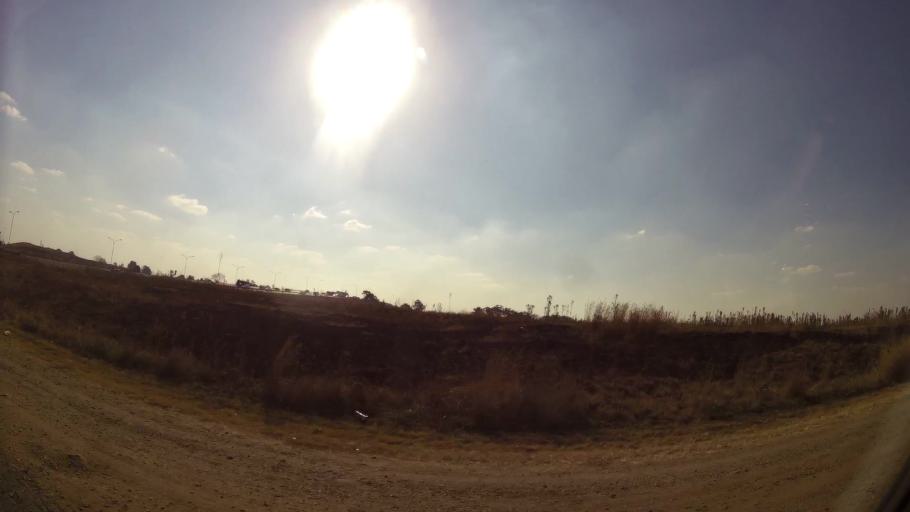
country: ZA
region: Gauteng
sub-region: Ekurhuleni Metropolitan Municipality
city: Benoni
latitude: -26.2229
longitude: 28.3207
